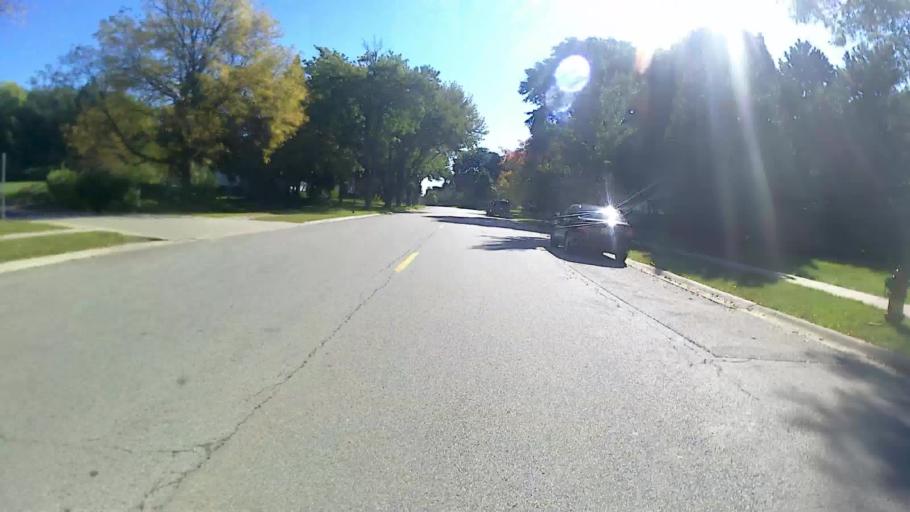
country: US
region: Illinois
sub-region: Cook County
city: Elk Grove Village
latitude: 42.0056
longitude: -87.9897
